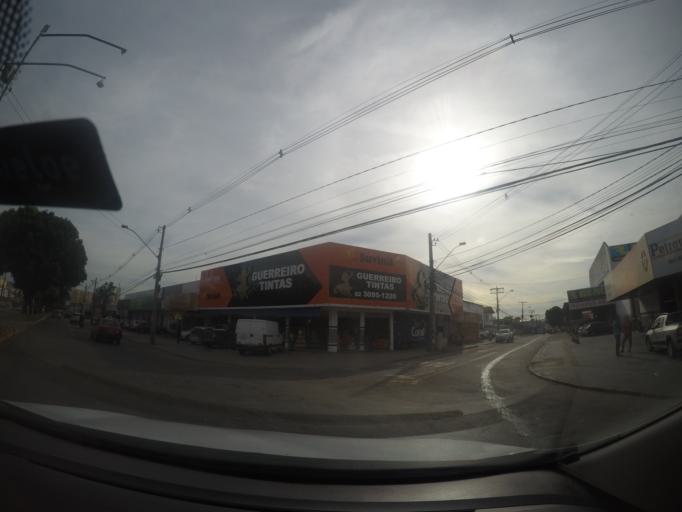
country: BR
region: Goias
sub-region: Goiania
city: Goiania
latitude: -16.6757
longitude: -49.3065
